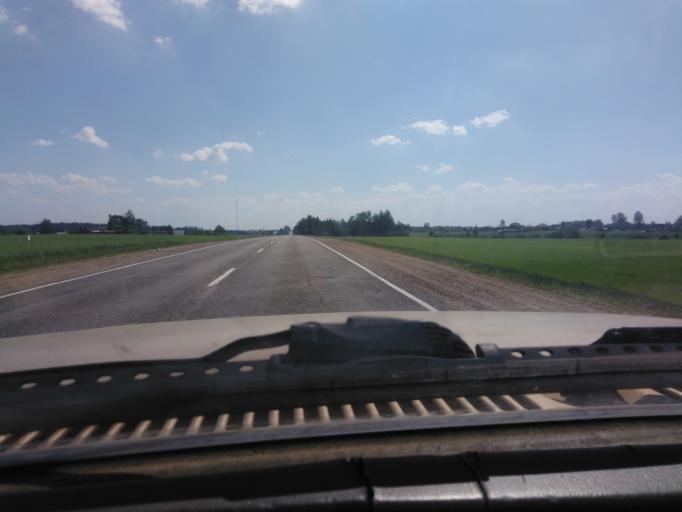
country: BY
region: Mogilev
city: Kamyennyya Lavy
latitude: 54.0399
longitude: 30.3245
